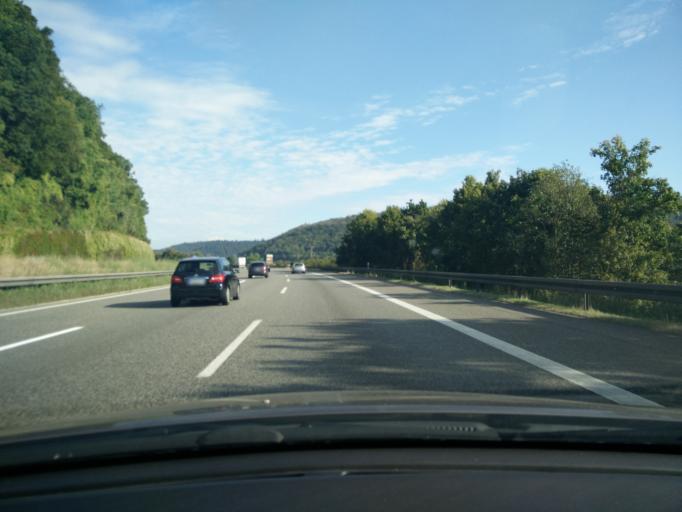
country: DE
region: Bavaria
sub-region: Regierungsbezirk Mittelfranken
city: Greding
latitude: 49.0228
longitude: 11.3676
